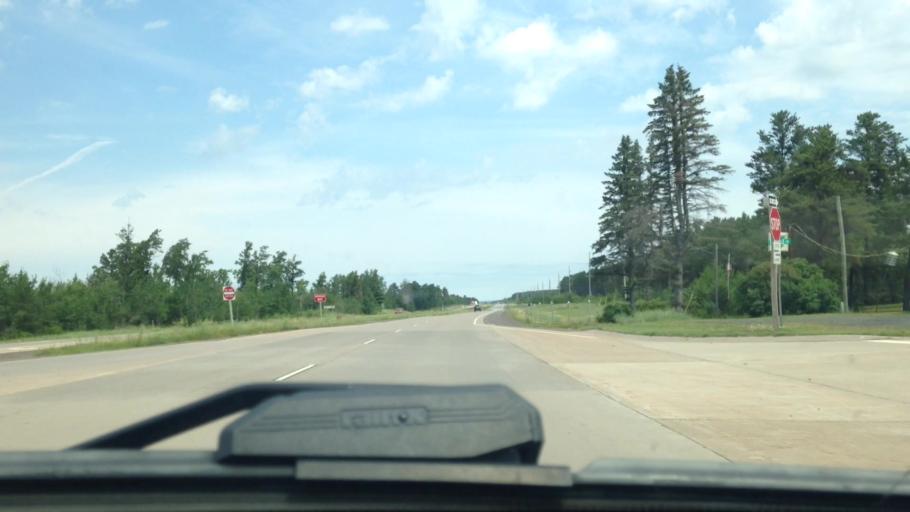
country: US
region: Wisconsin
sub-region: Douglas County
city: Lake Nebagamon
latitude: 46.2878
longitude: -91.8112
